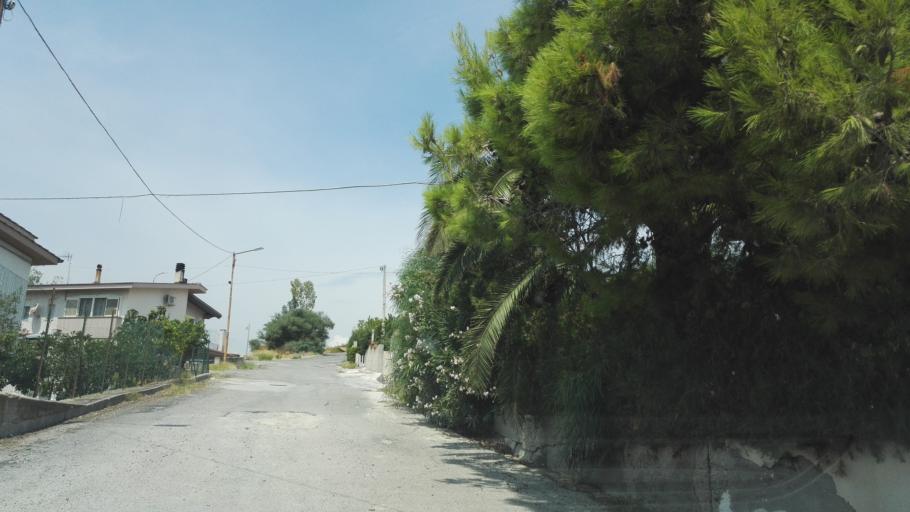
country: IT
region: Calabria
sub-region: Provincia di Reggio Calabria
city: Riace Marina
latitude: 38.3913
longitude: 16.5257
